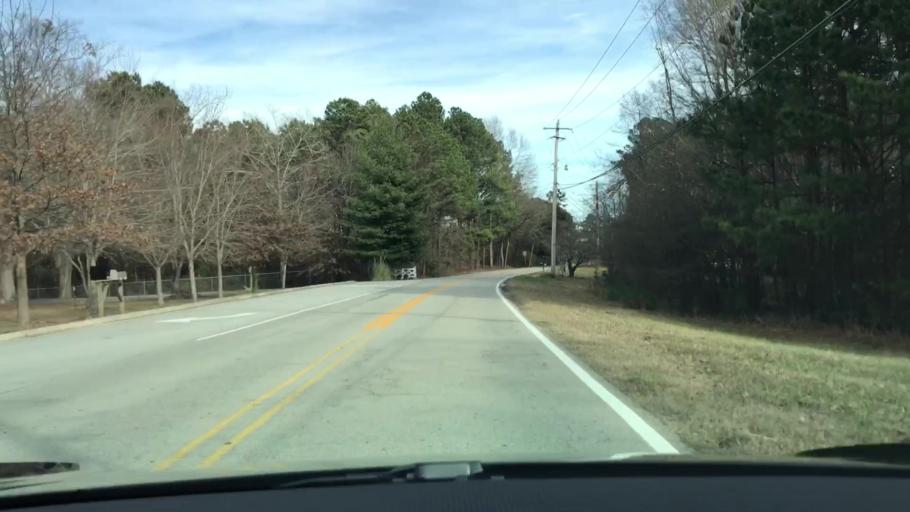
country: US
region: Georgia
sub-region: Gwinnett County
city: Buford
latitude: 34.1445
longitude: -83.9845
